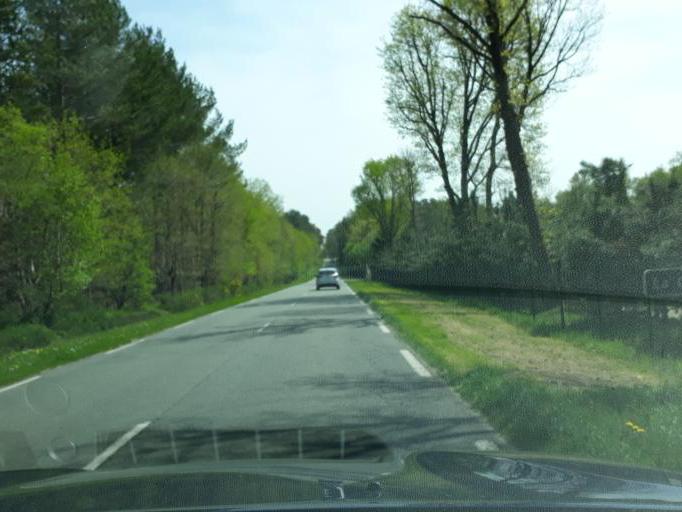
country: FR
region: Ile-de-France
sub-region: Departement des Yvelines
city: Saint-Leger-en-Yvelines
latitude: 48.6853
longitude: 1.7743
